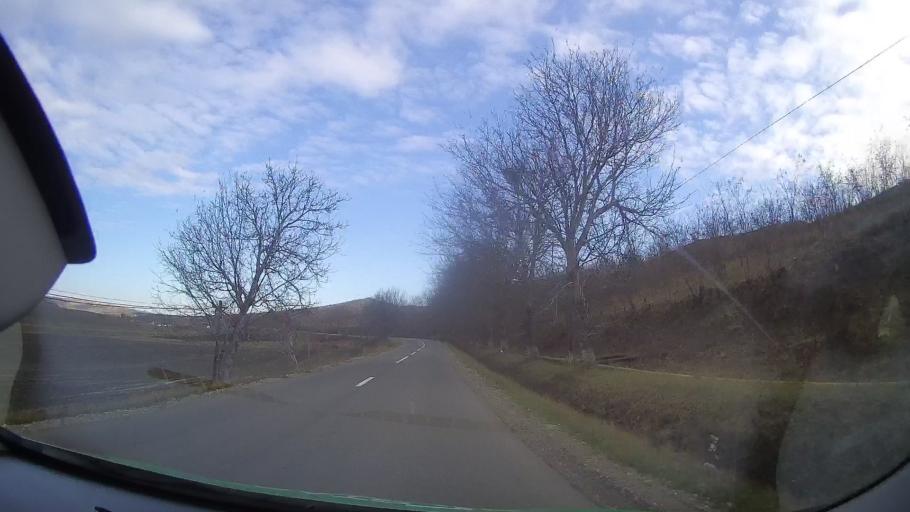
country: RO
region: Mures
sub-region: Comuna Iclanzel
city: Iclanzel
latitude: 46.5088
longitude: 24.2663
